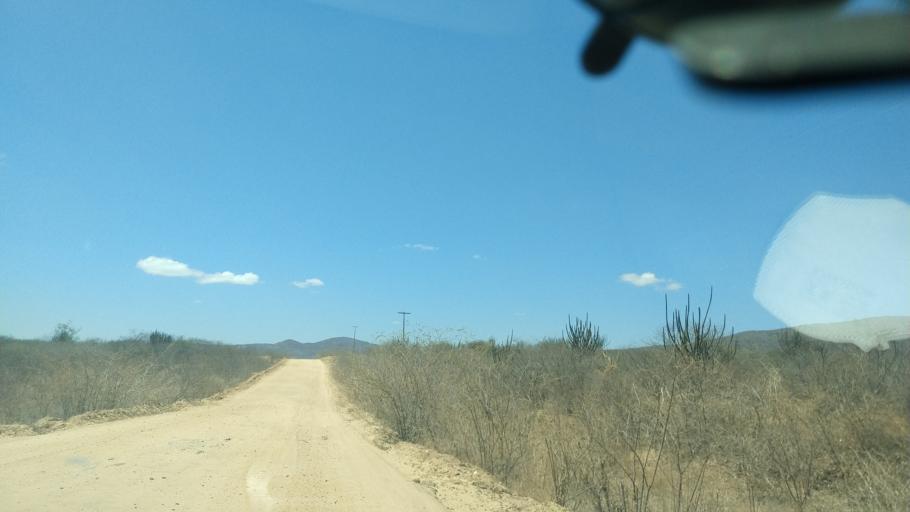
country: BR
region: Rio Grande do Norte
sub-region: Sao Tome
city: Sao Tome
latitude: -5.9744
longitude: -36.1677
